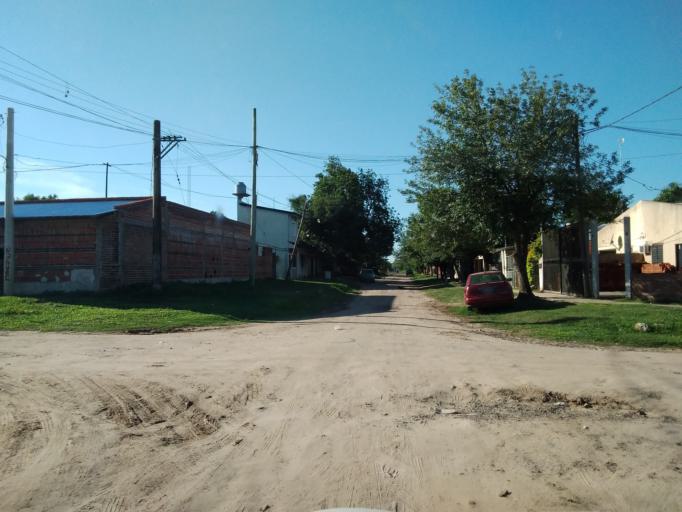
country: AR
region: Corrientes
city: Corrientes
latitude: -27.5036
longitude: -58.7808
